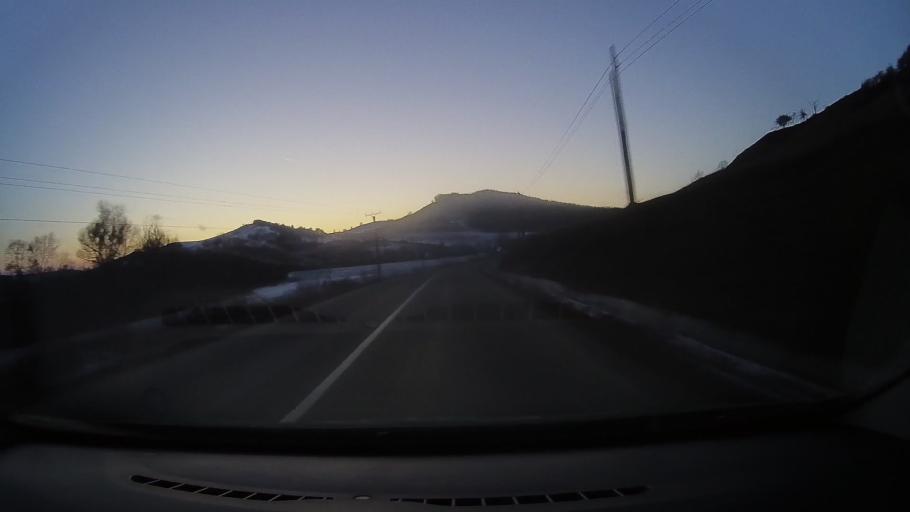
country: RO
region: Sibiu
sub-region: Comuna Alma
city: Alma
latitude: 46.2035
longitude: 24.4586
